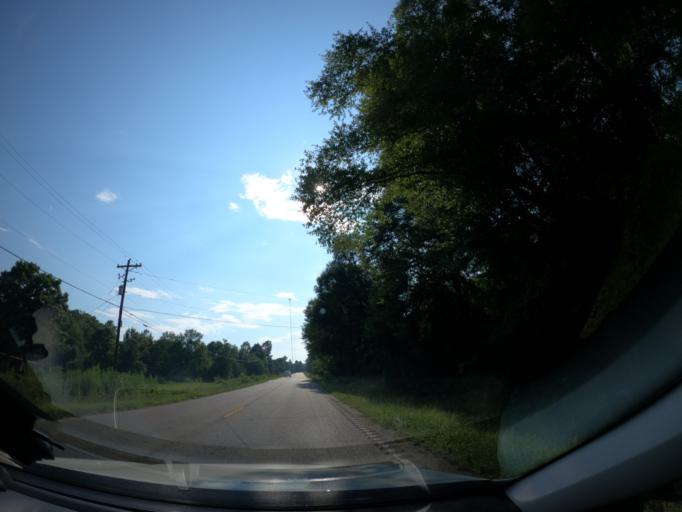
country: US
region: South Carolina
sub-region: Aiken County
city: Jackson
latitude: 33.4091
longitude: -81.8177
